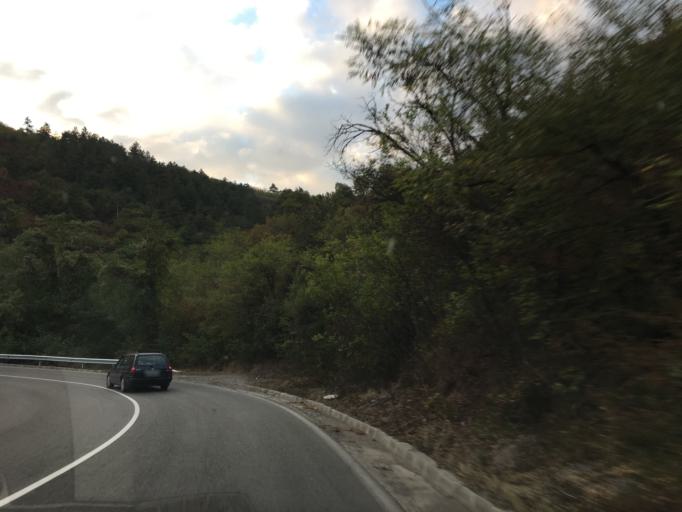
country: BG
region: Sofiya
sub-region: Obshtina Svoge
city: Svoge
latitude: 42.8411
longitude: 23.3609
